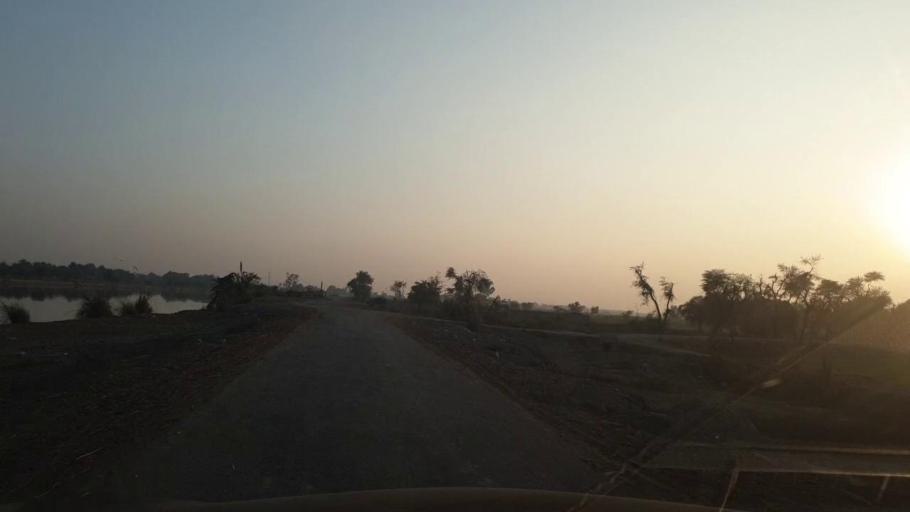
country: PK
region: Sindh
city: Ubauro
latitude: 28.2673
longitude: 69.7790
